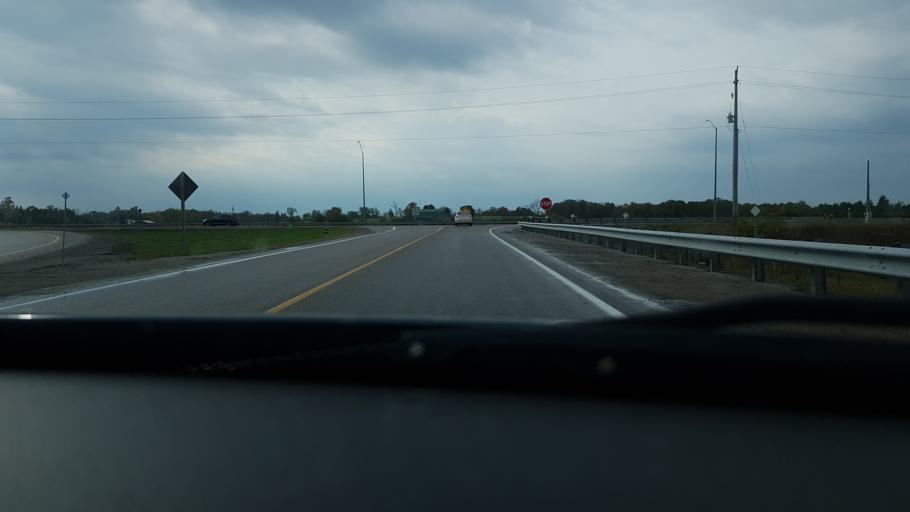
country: CA
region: Ontario
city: Omemee
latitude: 44.4863
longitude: -78.7600
